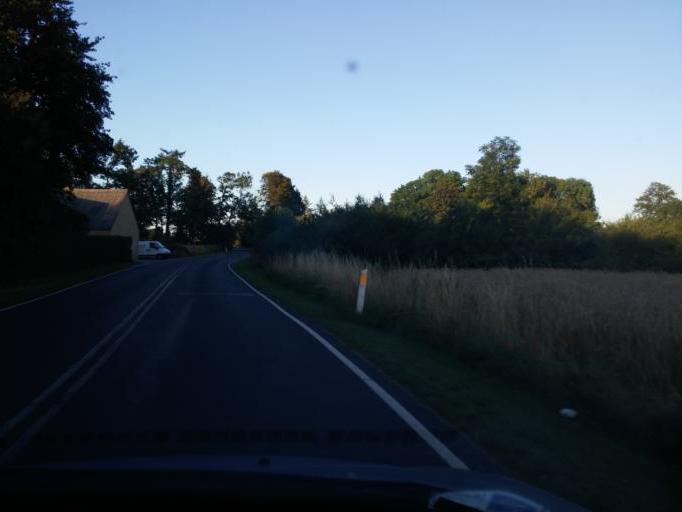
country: DK
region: South Denmark
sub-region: Kerteminde Kommune
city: Langeskov
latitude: 55.4051
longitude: 10.5572
